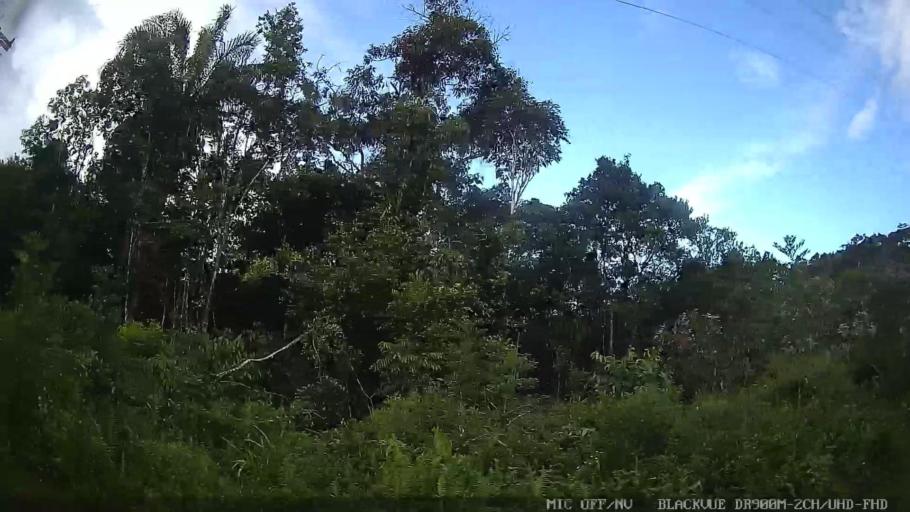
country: BR
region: Sao Paulo
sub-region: Peruibe
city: Peruibe
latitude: -24.1850
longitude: -46.9405
